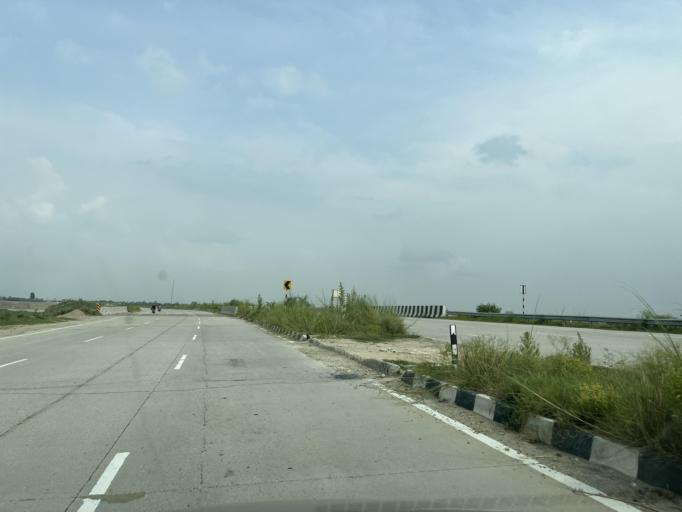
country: IN
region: Uttarakhand
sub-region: Udham Singh Nagar
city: Bazpur
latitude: 29.1468
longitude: 79.0304
